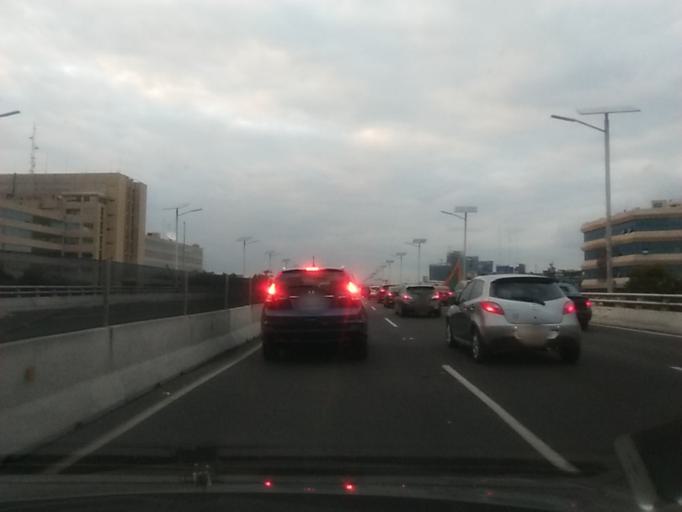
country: MX
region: Mexico City
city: Miguel Hidalgo
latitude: 19.4393
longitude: -99.2144
